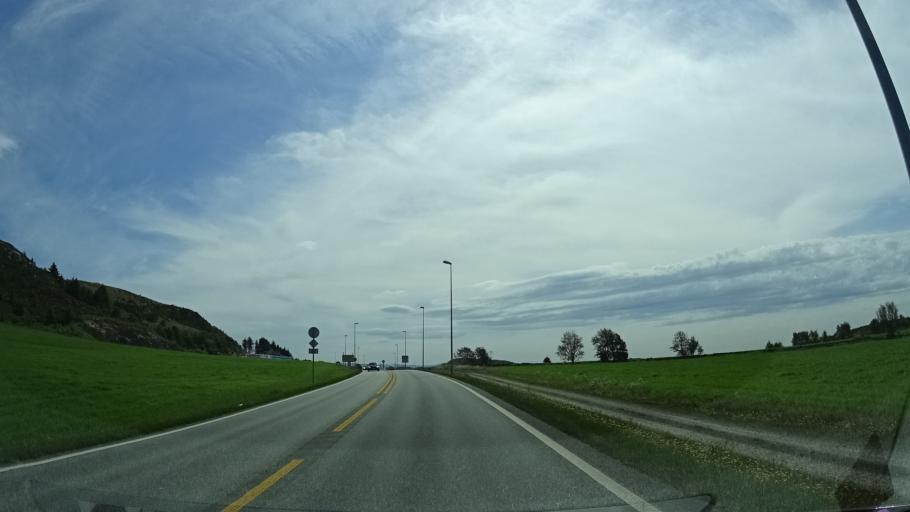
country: NO
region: Rogaland
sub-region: Rennesoy
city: Vikevag
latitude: 59.0664
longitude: 5.6738
